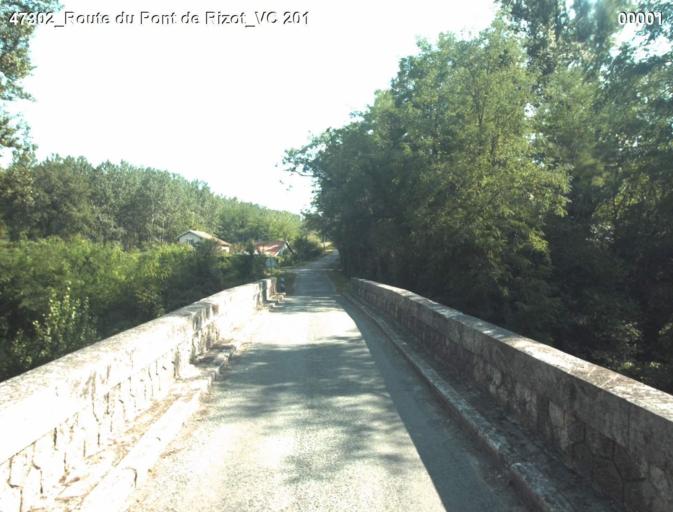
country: FR
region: Aquitaine
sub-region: Departement du Lot-et-Garonne
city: Mezin
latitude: 44.0396
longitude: 0.1951
